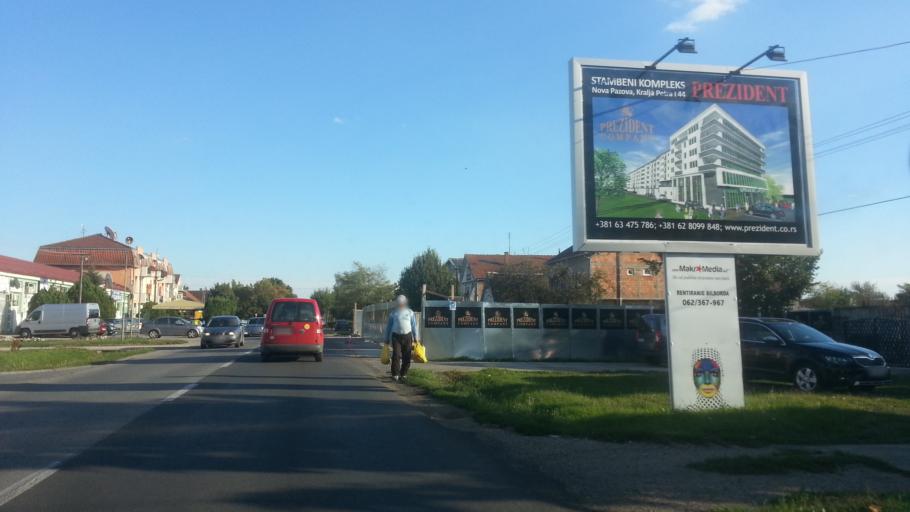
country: RS
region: Autonomna Pokrajina Vojvodina
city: Nova Pazova
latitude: 44.9426
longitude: 20.2218
